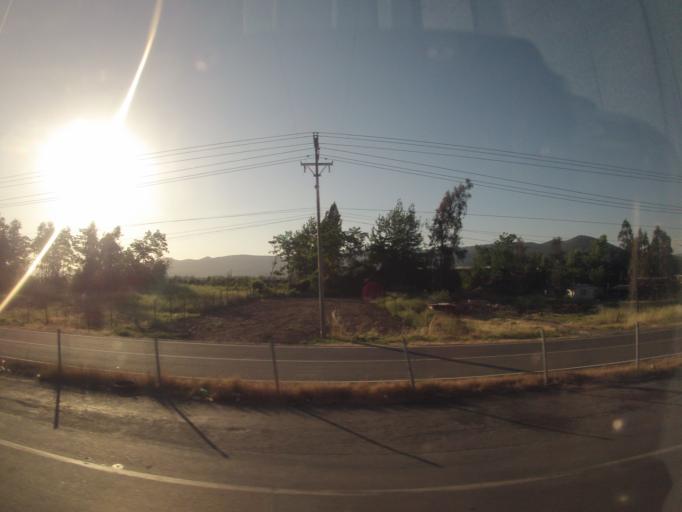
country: CL
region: O'Higgins
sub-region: Provincia de Colchagua
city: Chimbarongo
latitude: -34.7174
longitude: -71.0318
